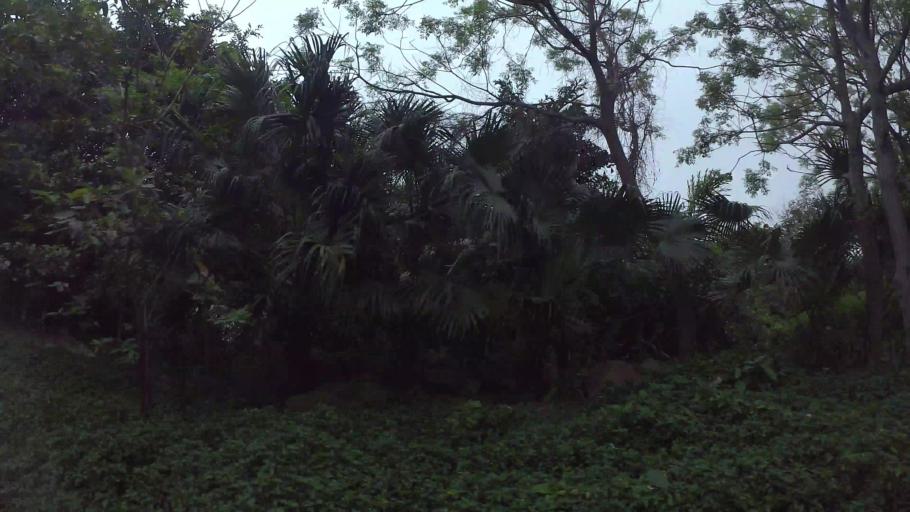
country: VN
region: Da Nang
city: Son Tra
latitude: 16.1166
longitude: 108.3082
